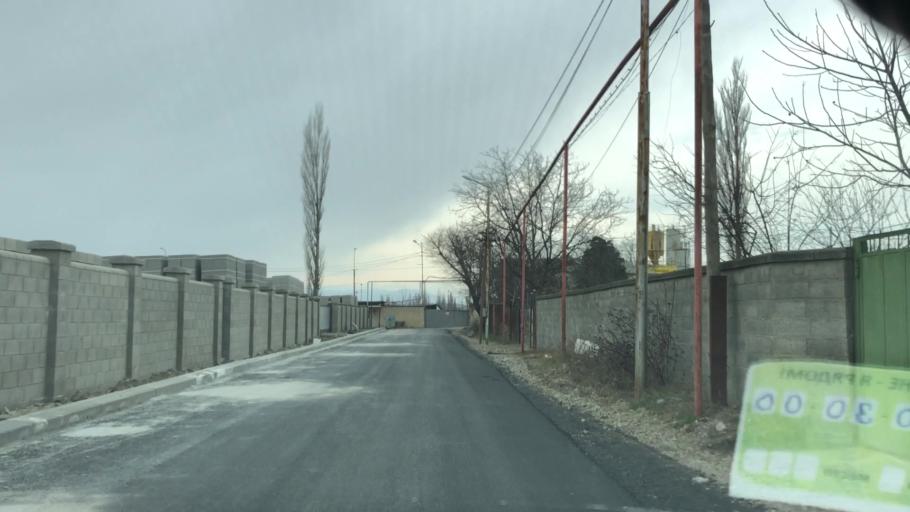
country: GE
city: Didi Lilo
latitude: 41.7013
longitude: 44.9255
